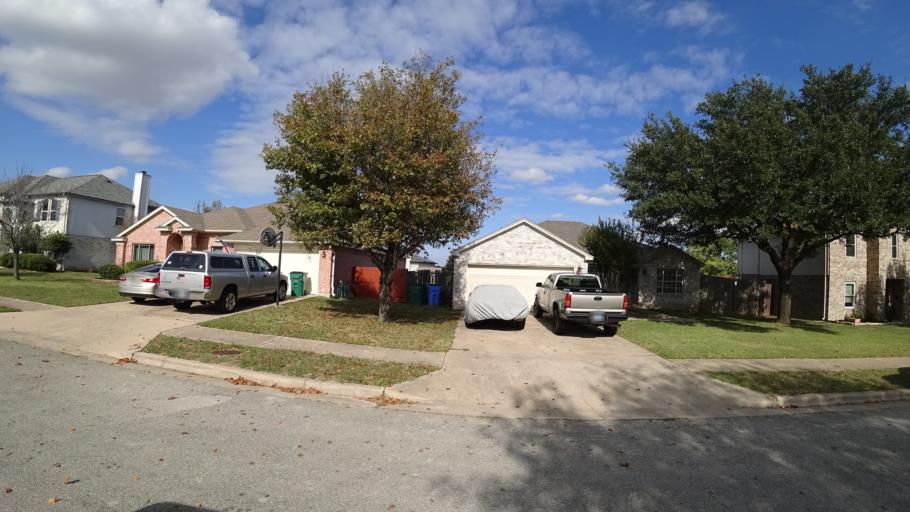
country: US
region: Texas
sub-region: Travis County
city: Pflugerville
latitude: 30.4359
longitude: -97.6342
